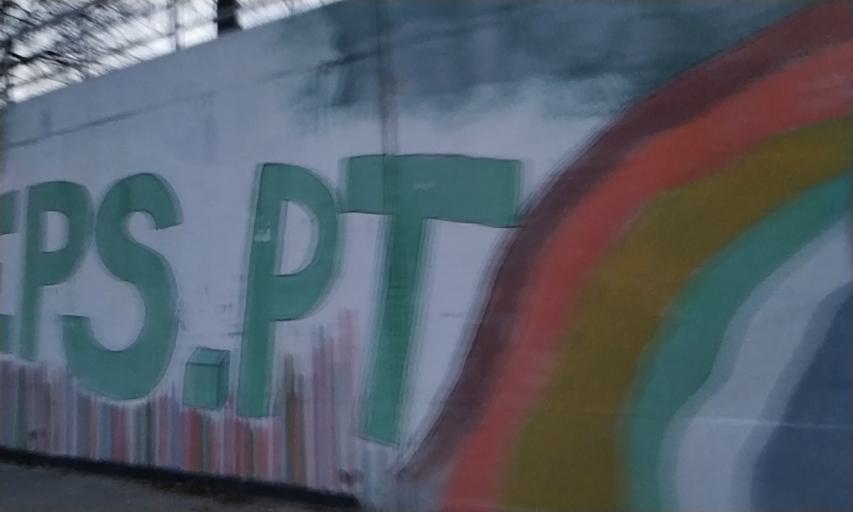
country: PT
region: Setubal
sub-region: Setubal
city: Setubal
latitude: 38.5216
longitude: -8.8471
